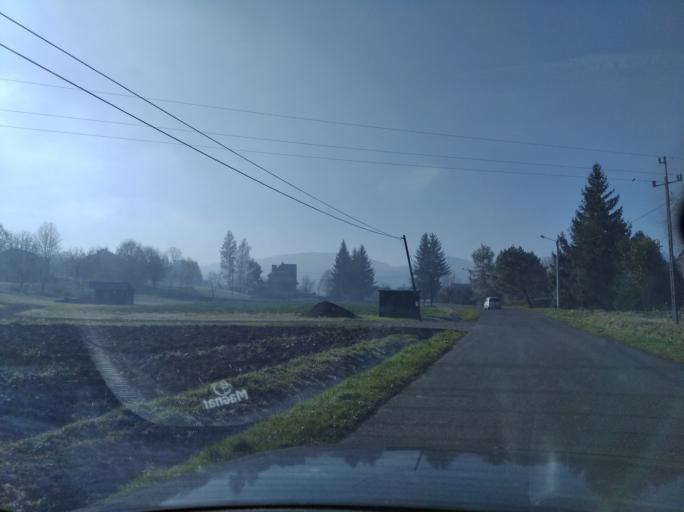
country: PL
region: Subcarpathian Voivodeship
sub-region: Powiat strzyzowski
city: Wysoka Strzyzowska
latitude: 49.8530
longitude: 21.7025
